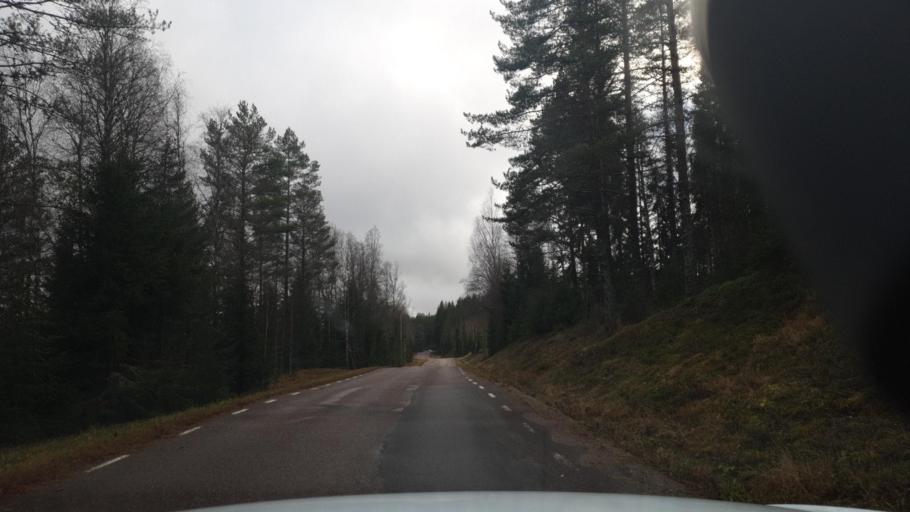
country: SE
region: Vaermland
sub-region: Arvika Kommun
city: Arvika
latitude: 59.8141
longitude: 12.8337
